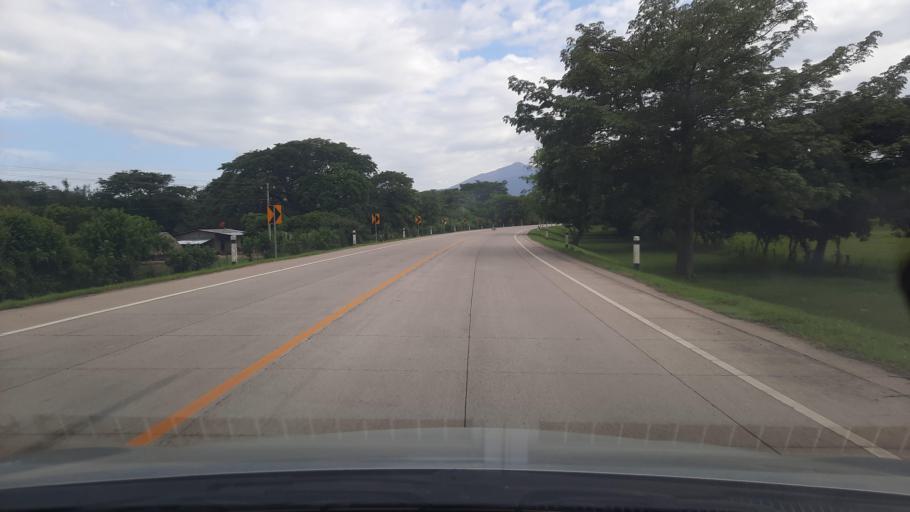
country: NI
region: Chinandega
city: Somotillo
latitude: 12.8190
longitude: -86.8991
